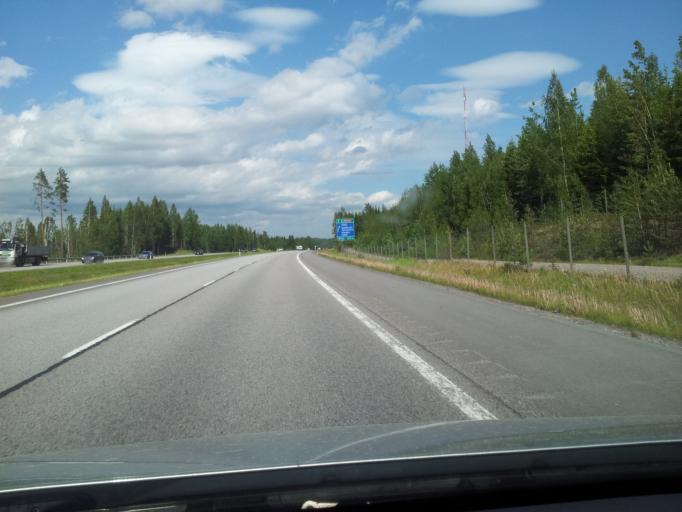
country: FI
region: Uusimaa
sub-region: Loviisa
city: Perna
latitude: 60.4775
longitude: 25.8689
